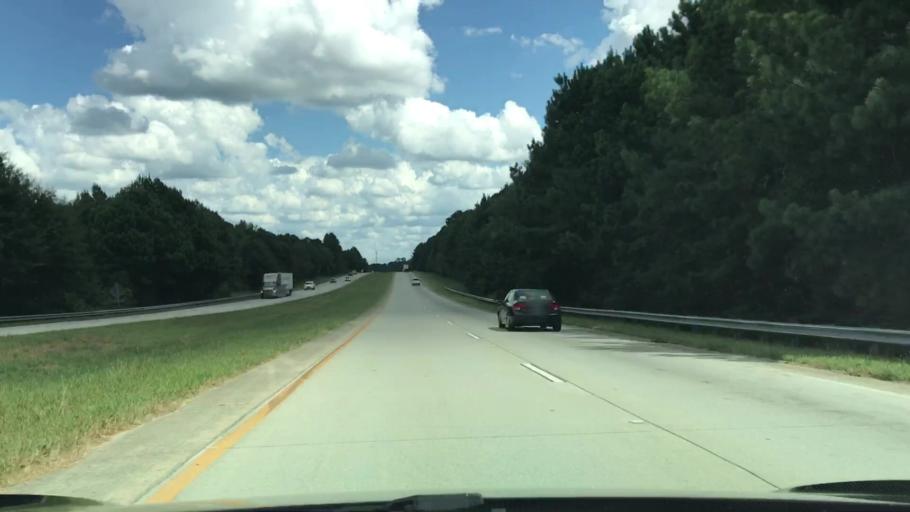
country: US
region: Georgia
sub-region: Oconee County
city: Bogart
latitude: 33.9210
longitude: -83.4988
